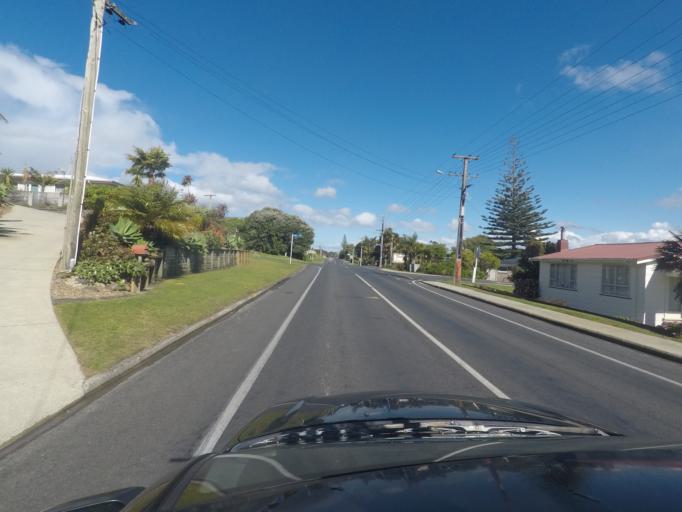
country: NZ
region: Bay of Plenty
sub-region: Western Bay of Plenty District
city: Waihi Beach
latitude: -37.4148
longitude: 175.9474
